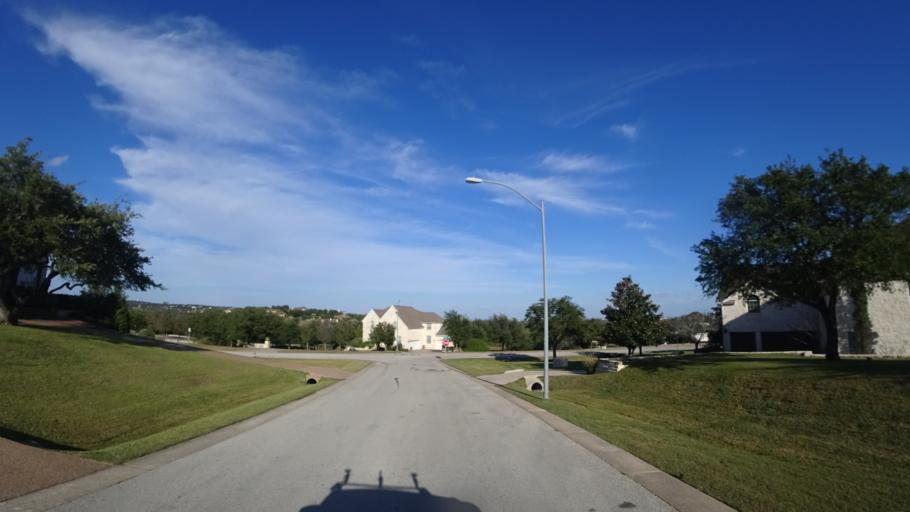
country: US
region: Texas
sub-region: Travis County
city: Barton Creek
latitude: 30.2590
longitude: -97.8444
